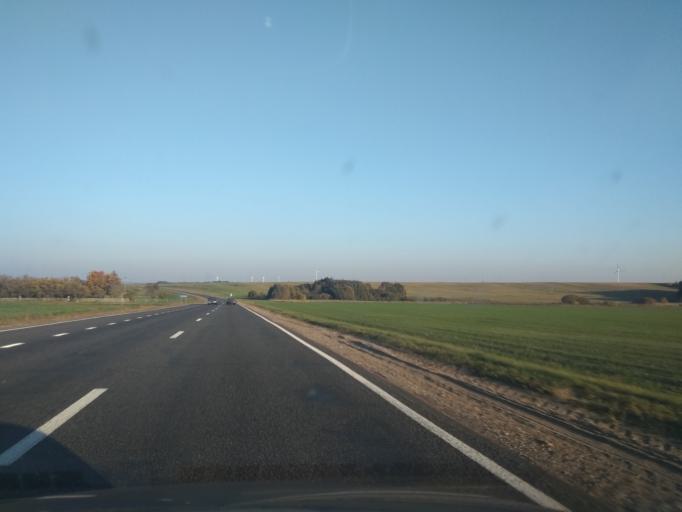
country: BY
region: Grodnenskaya
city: Zel'va
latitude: 53.1375
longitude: 24.7224
